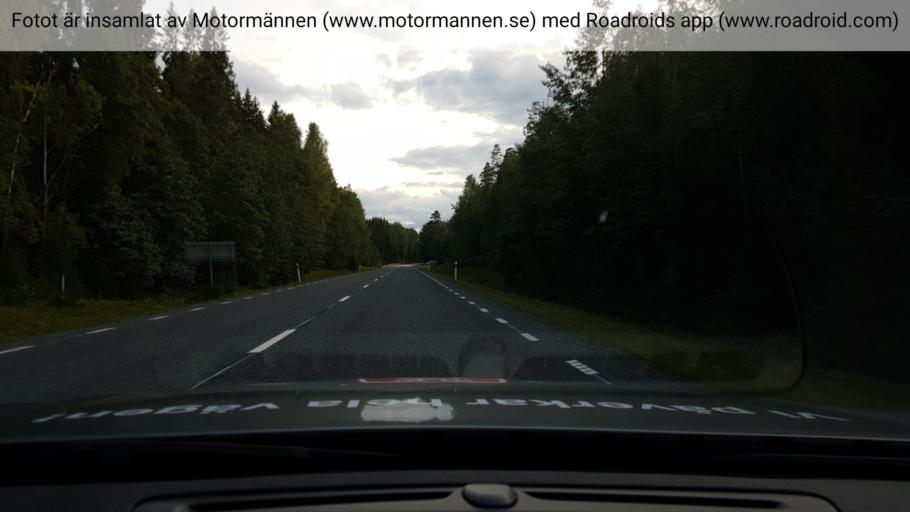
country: SE
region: OErebro
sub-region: Hallefors Kommun
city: Haellefors
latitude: 59.7939
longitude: 14.5460
